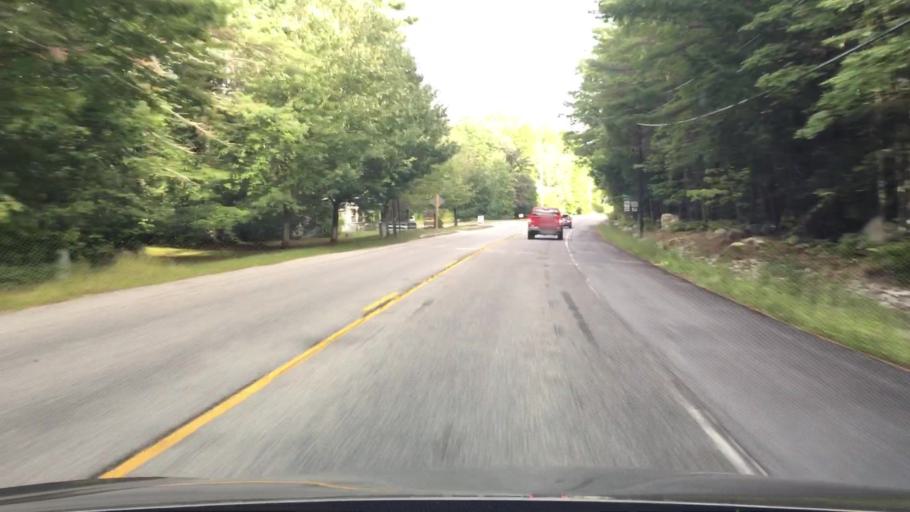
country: US
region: Maine
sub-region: Cumberland County
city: Bridgton
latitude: 44.0630
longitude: -70.7365
